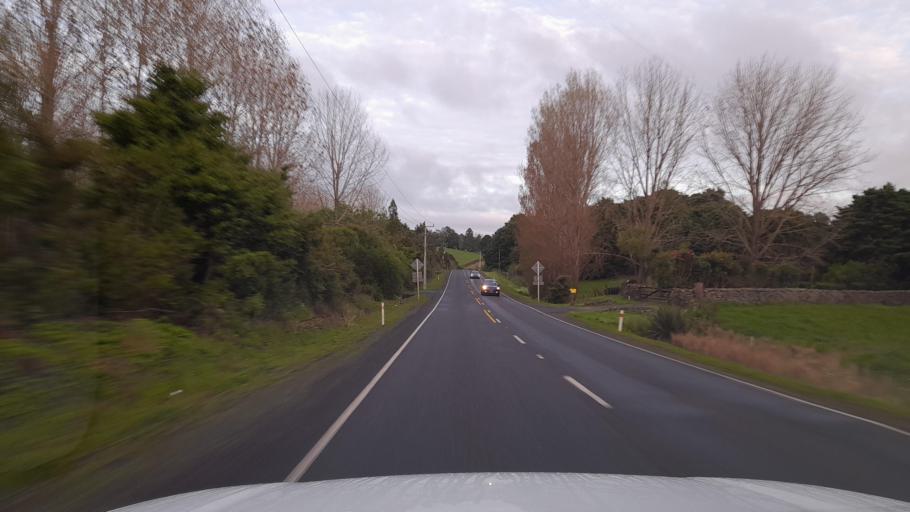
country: NZ
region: Northland
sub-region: Whangarei
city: Maungatapere
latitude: -35.7556
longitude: 174.1784
